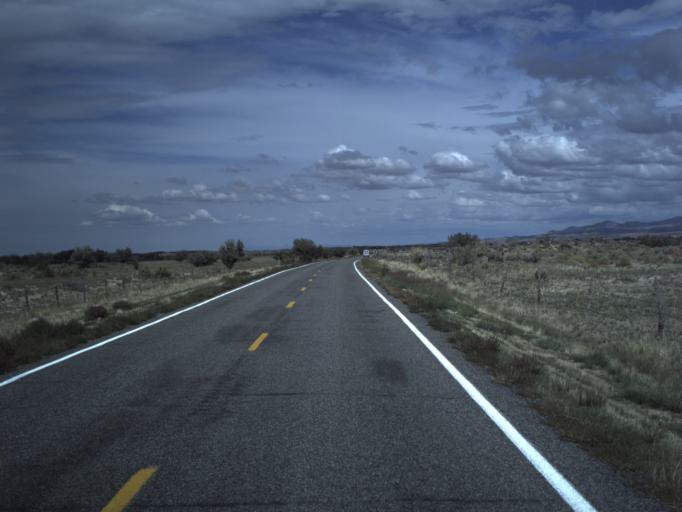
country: US
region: Utah
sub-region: Millard County
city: Fillmore
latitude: 39.0998
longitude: -112.4101
